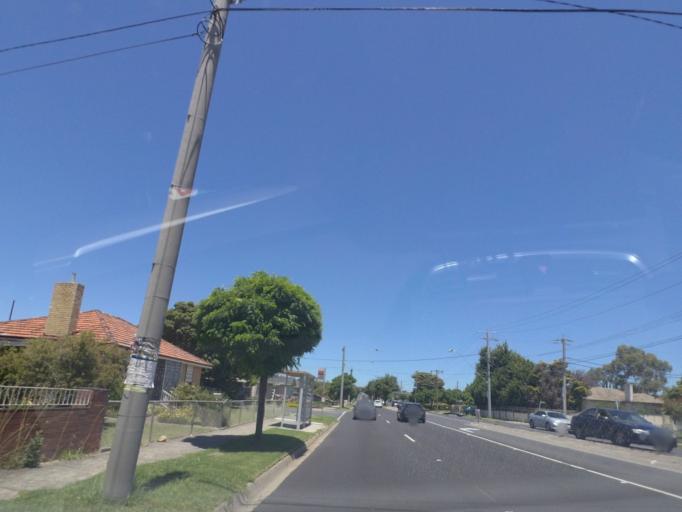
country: AU
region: Victoria
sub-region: Darebin
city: Kingsbury
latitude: -37.7286
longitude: 145.0259
